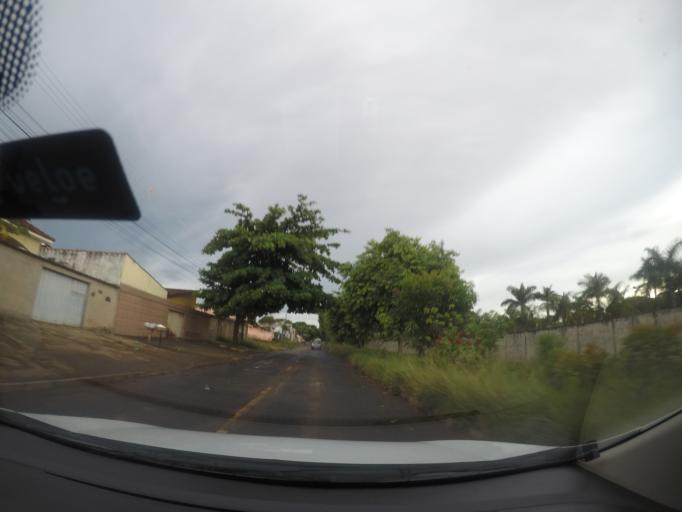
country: BR
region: Goias
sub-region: Goiania
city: Goiania
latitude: -16.7267
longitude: -49.3099
